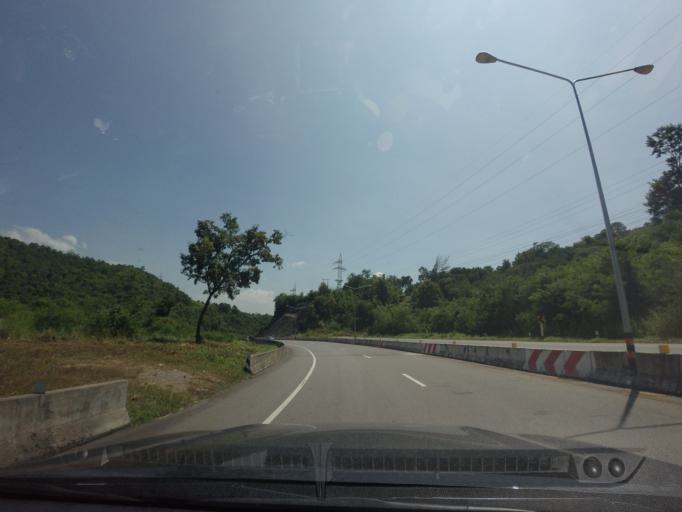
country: TH
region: Phetchabun
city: Lom Sak
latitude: 16.7671
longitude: 101.1381
